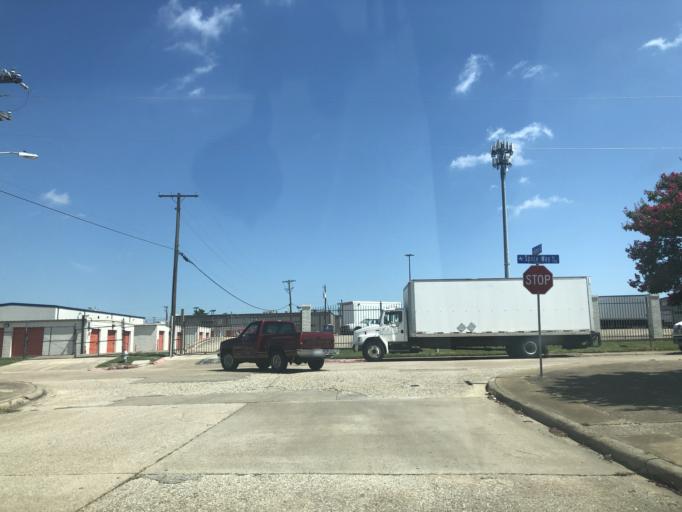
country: US
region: Texas
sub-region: Dallas County
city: Duncanville
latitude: 32.6447
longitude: -96.9238
